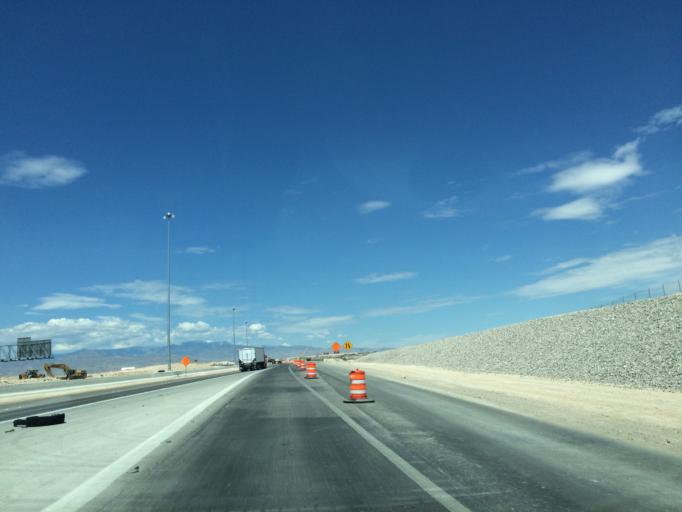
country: US
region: Nevada
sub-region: Clark County
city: Nellis Air Force Base
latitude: 36.2925
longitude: -115.1386
